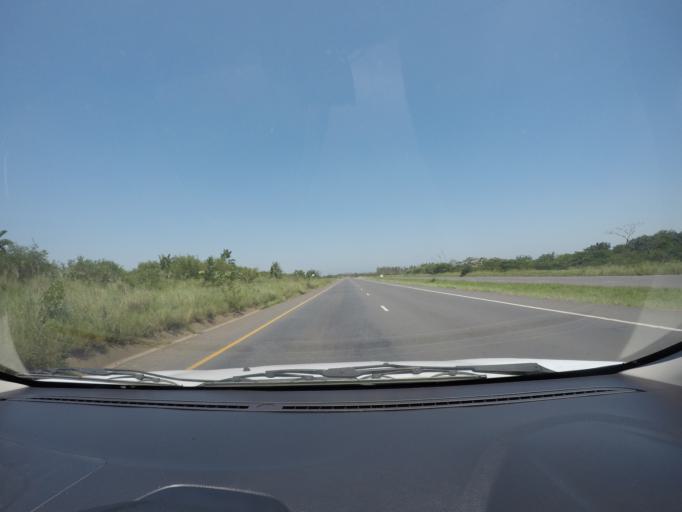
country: ZA
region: KwaZulu-Natal
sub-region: uThungulu District Municipality
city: Richards Bay
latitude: -28.7784
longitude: 31.9696
